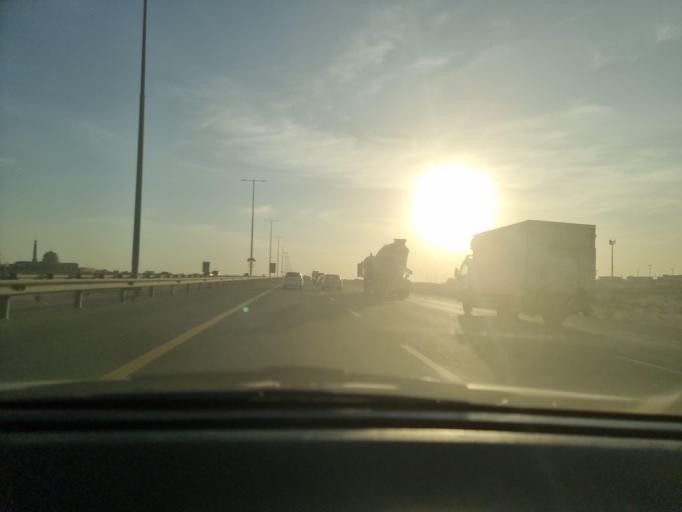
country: AE
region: Abu Dhabi
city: Abu Dhabi
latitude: 24.3309
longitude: 54.6937
